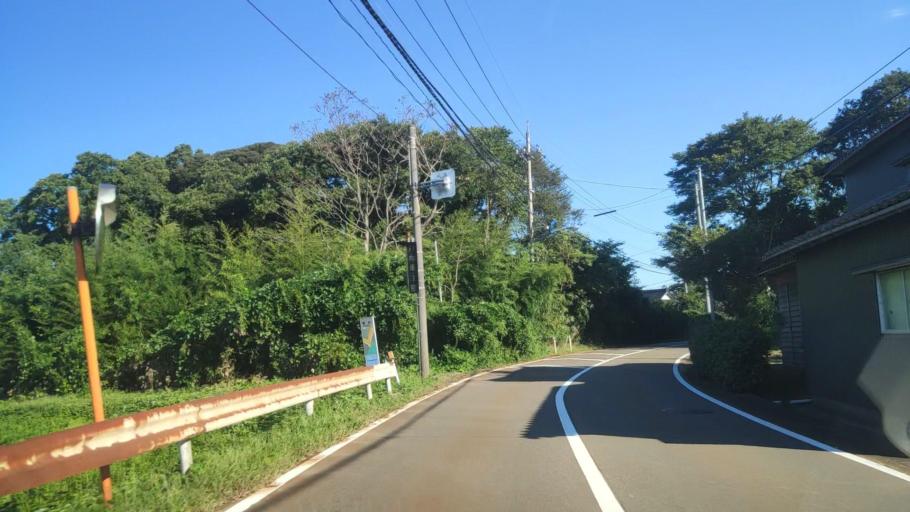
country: JP
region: Ishikawa
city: Hakui
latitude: 36.8293
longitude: 136.7586
